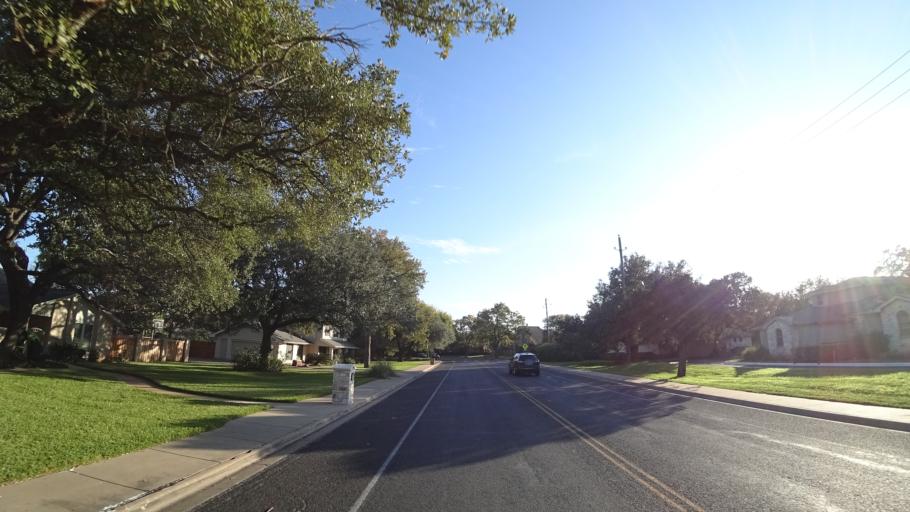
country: US
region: Texas
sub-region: Williamson County
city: Anderson Mill
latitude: 30.4440
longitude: -97.8063
